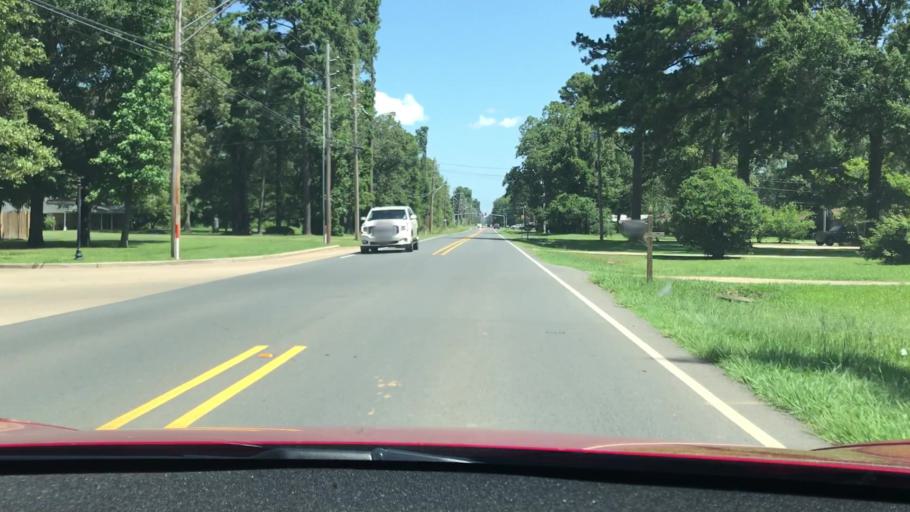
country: US
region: Louisiana
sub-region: De Soto Parish
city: Stonewall
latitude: 32.3516
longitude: -93.7138
